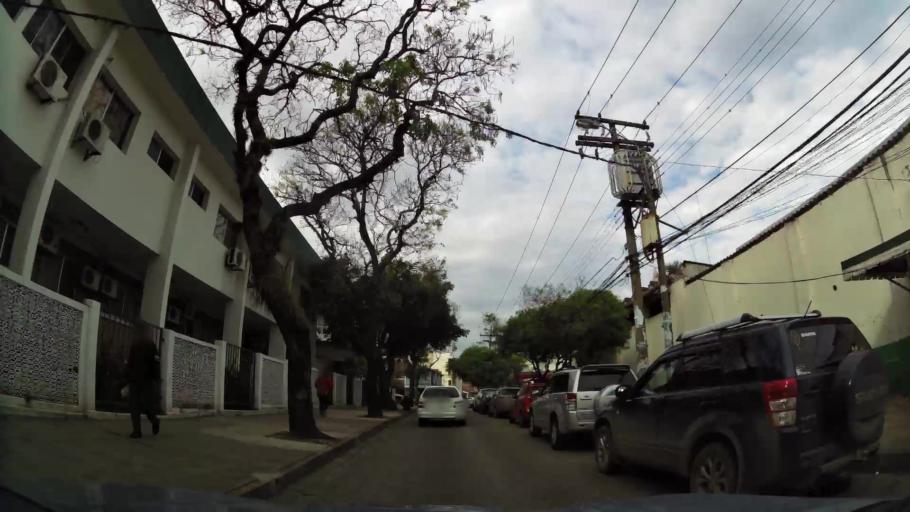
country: BO
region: Santa Cruz
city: Santa Cruz de la Sierra
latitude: -17.7780
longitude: -63.1860
